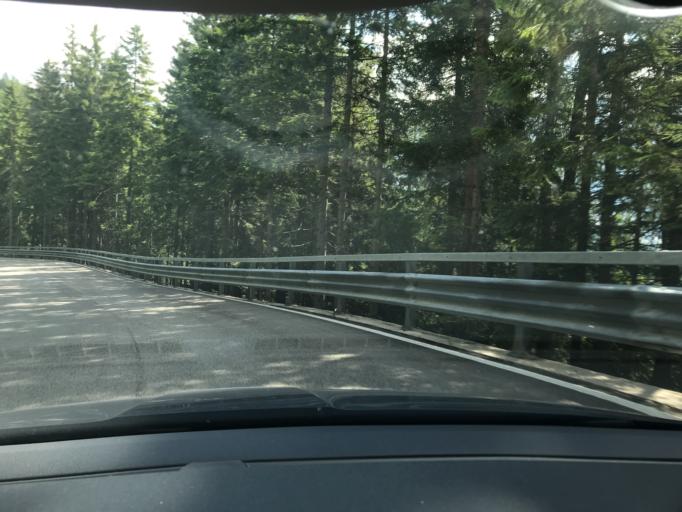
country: IT
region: Veneto
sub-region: Provincia di Belluno
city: Cortina d'Ampezzo
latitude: 46.5219
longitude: 12.1147
